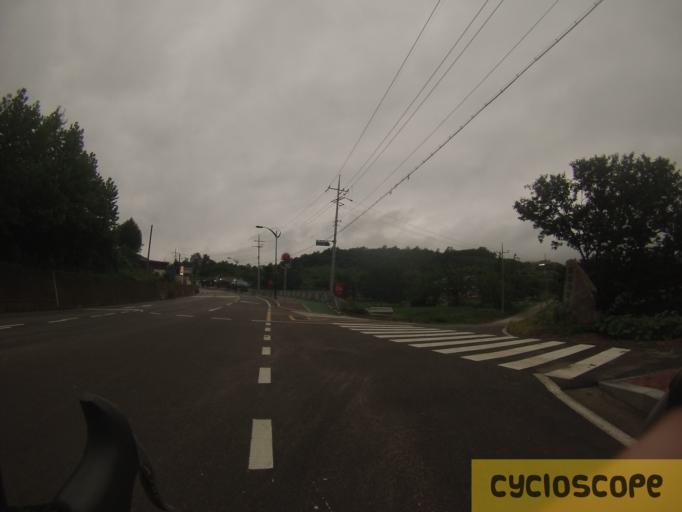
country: KR
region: Chungcheongnam-do
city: Yesan
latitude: 36.7478
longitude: 126.8731
